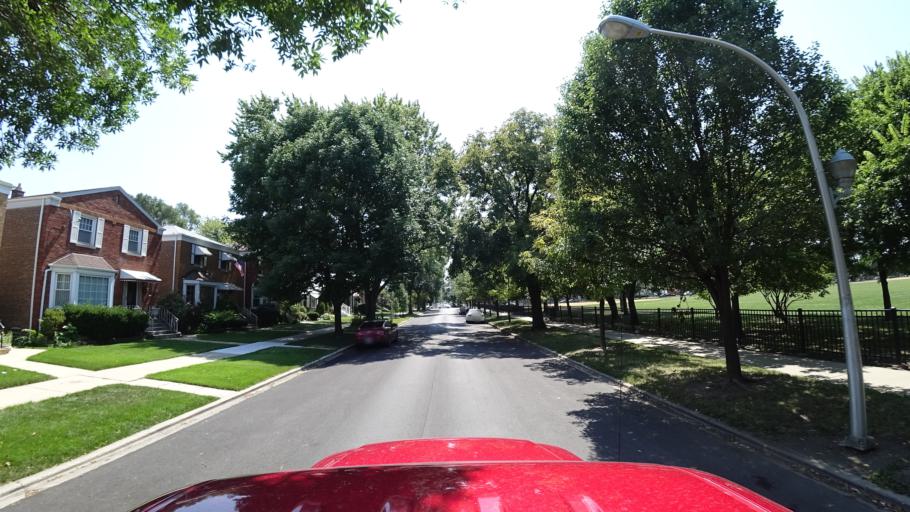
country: US
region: Illinois
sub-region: Cook County
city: Hometown
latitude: 41.7725
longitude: -87.7275
